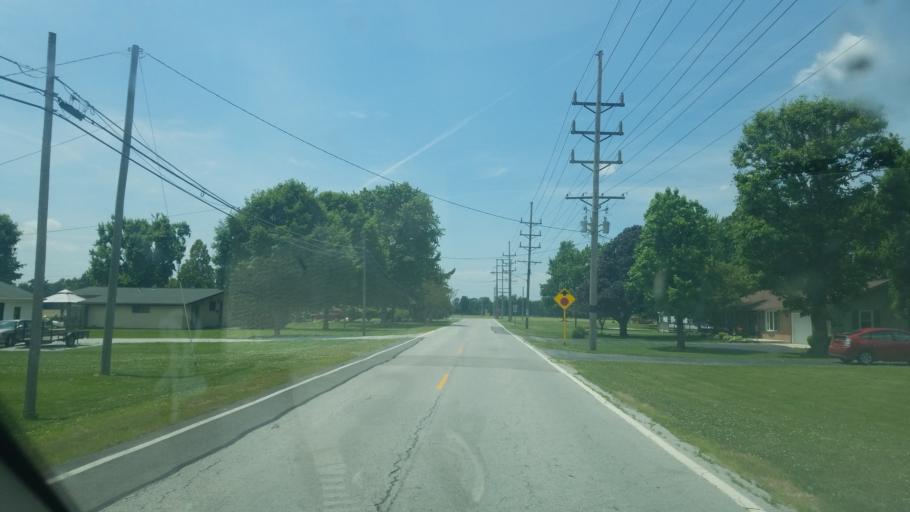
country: US
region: Ohio
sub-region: Hancock County
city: Arlington
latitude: 40.7831
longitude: -83.6495
